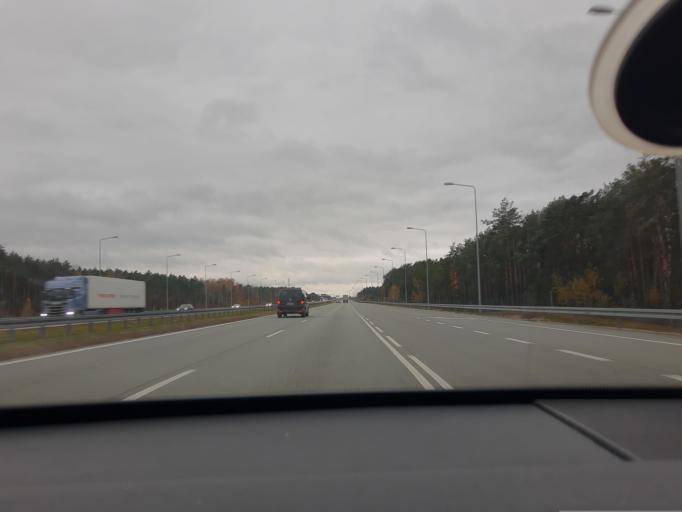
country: PL
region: Lodz Voivodeship
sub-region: Powiat pabianicki
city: Dobron
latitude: 51.5990
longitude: 19.2679
